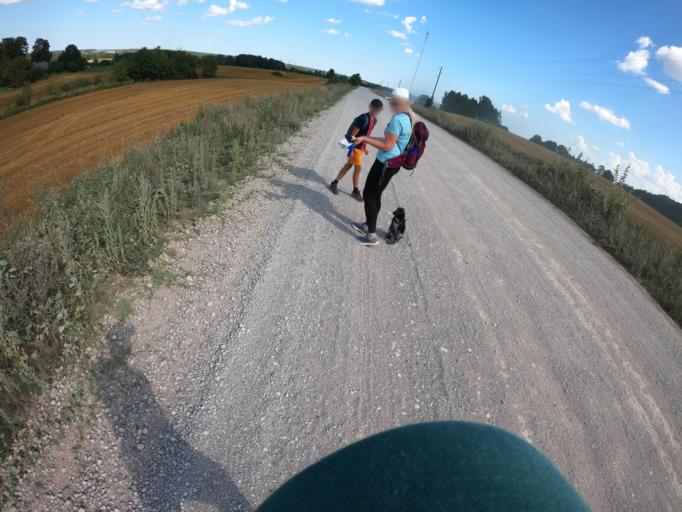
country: LV
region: Priekule
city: Priekule
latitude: 56.3610
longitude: 21.5567
